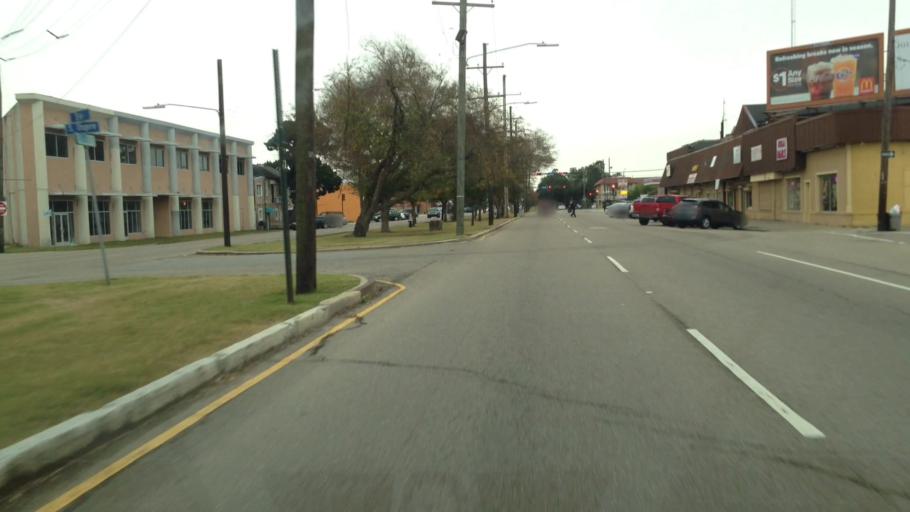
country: US
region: Louisiana
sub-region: Orleans Parish
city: New Orleans
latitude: 29.9528
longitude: -90.1017
